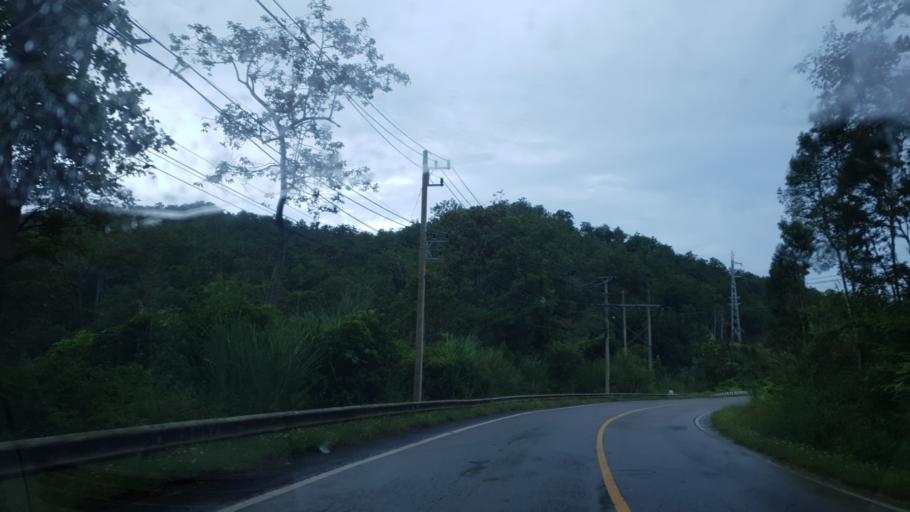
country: TH
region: Mae Hong Son
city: Ban Huai I Huak
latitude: 18.1387
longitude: 98.1940
